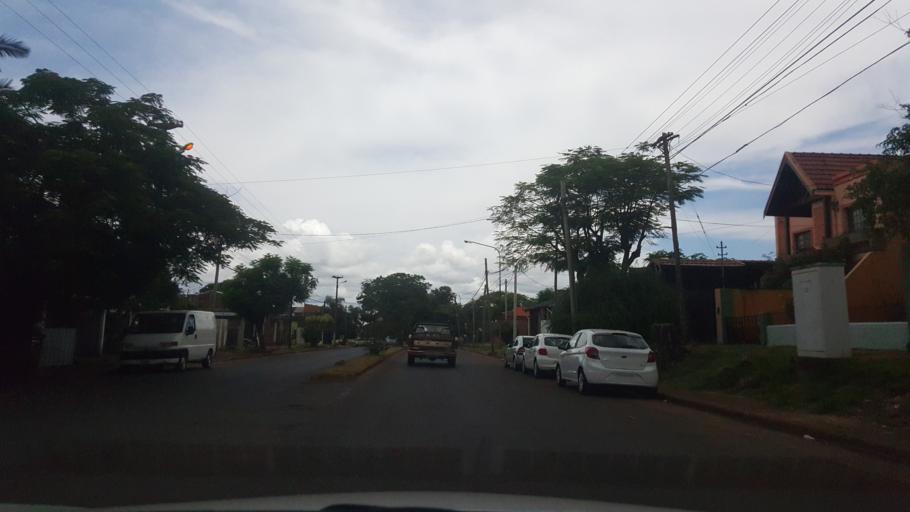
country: AR
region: Misiones
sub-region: Departamento de Capital
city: Posadas
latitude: -27.3980
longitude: -55.8999
